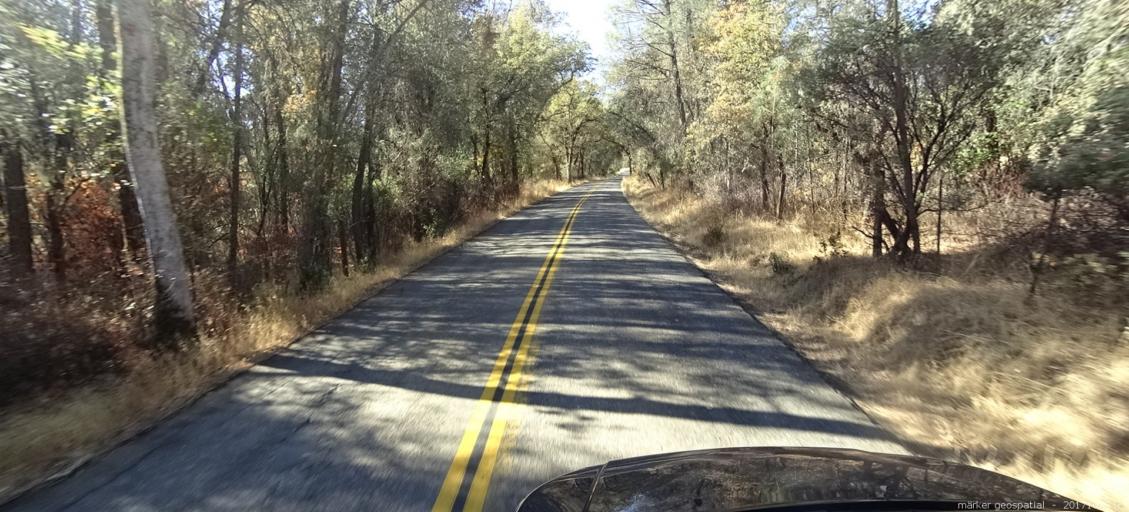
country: US
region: California
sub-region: Trinity County
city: Lewiston
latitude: 40.4255
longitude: -122.7305
